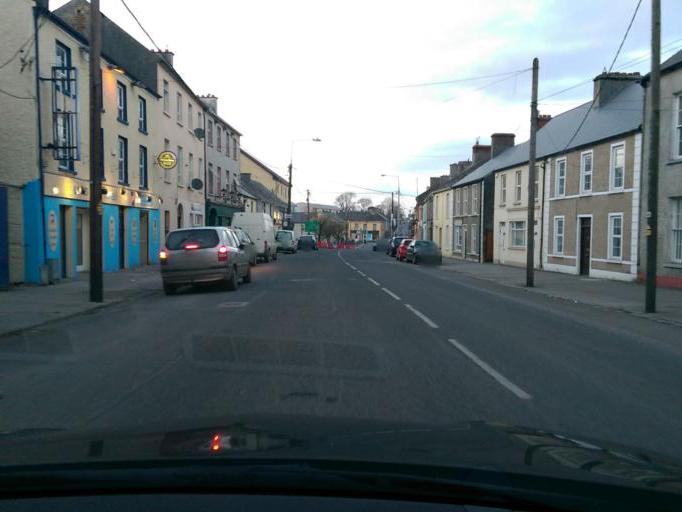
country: IE
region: Connaught
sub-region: County Galway
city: Portumna
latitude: 52.9964
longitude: -8.1273
